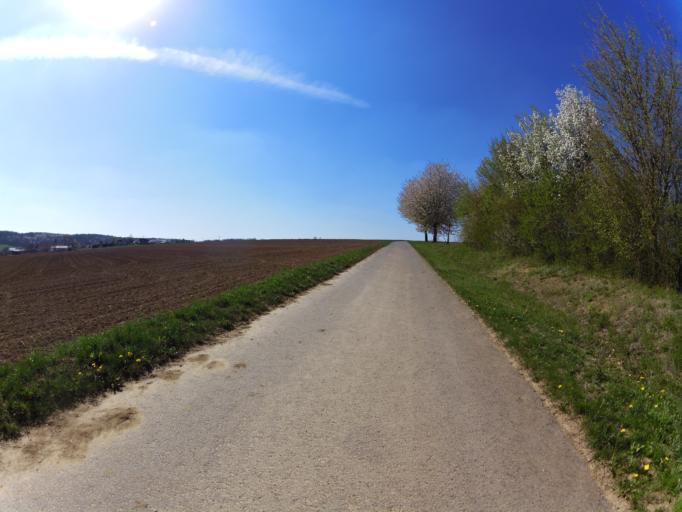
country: DE
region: Bavaria
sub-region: Regierungsbezirk Unterfranken
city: Kurnach
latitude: 49.8618
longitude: 10.0189
